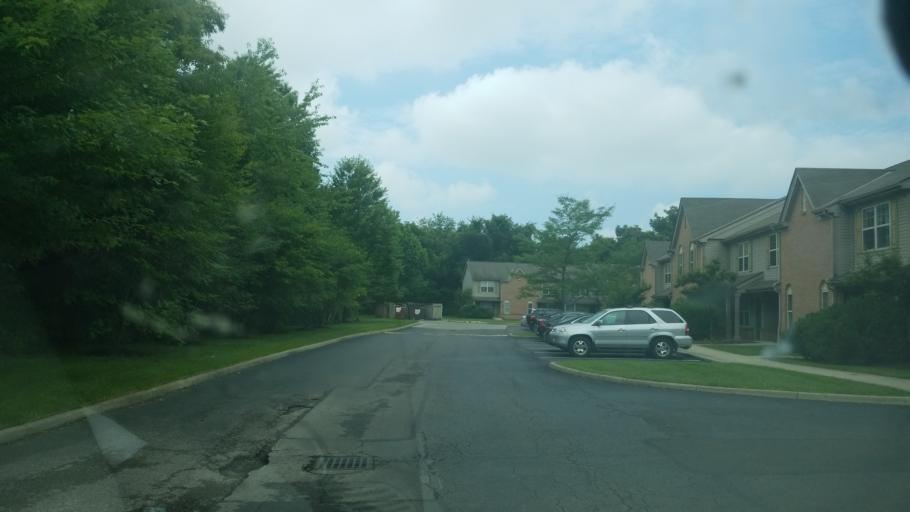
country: US
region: Ohio
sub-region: Franklin County
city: Reynoldsburg
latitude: 40.0004
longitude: -82.7985
